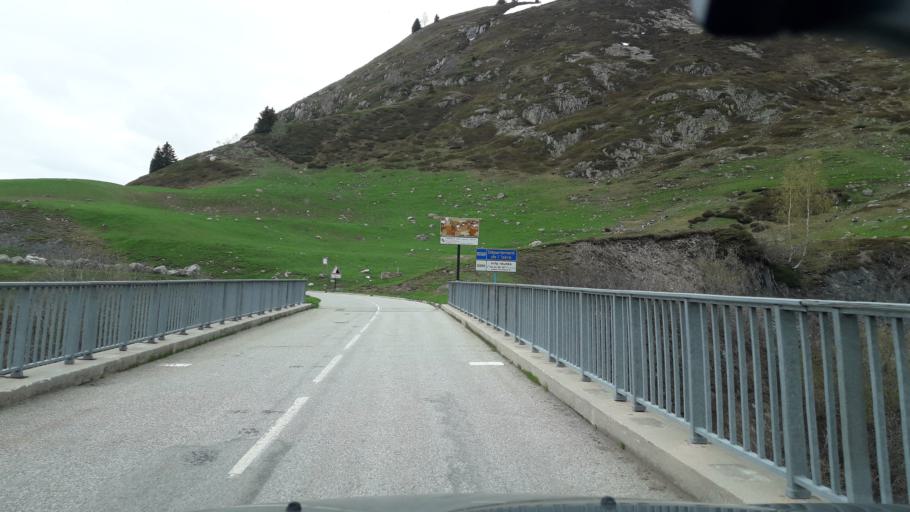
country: FR
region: Rhone-Alpes
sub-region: Departement de l'Isere
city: Theys
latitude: 45.2245
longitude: 6.1392
